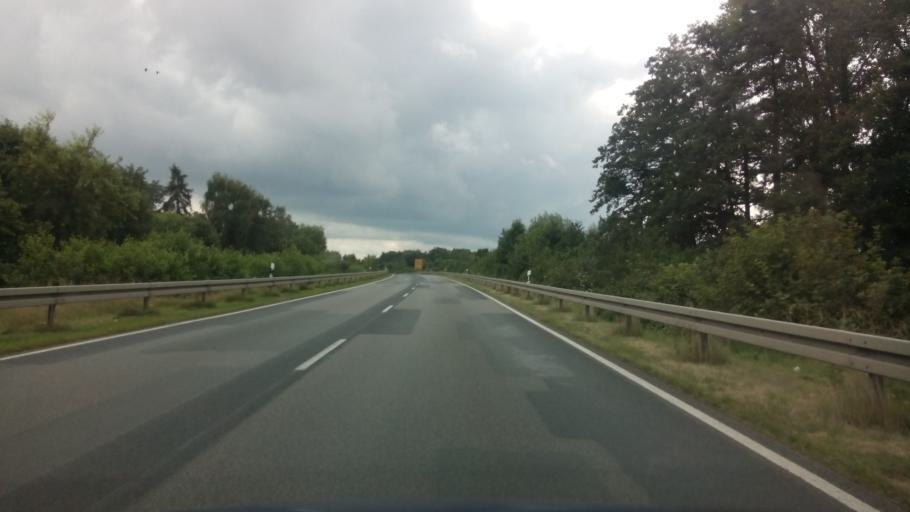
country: DE
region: Lower Saxony
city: Diepholz
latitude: 52.6159
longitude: 8.3622
